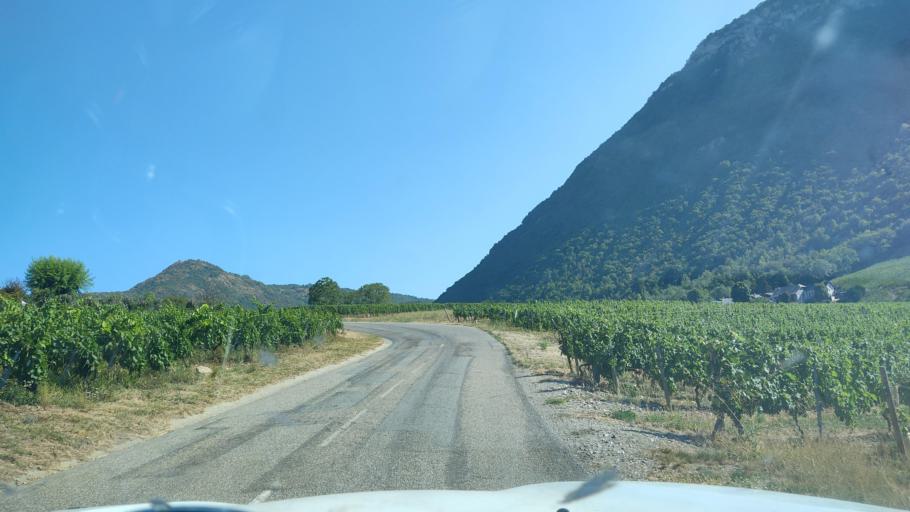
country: FR
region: Rhone-Alpes
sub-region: Departement de la Savoie
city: Les Marches
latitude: 45.5295
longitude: 6.0065
